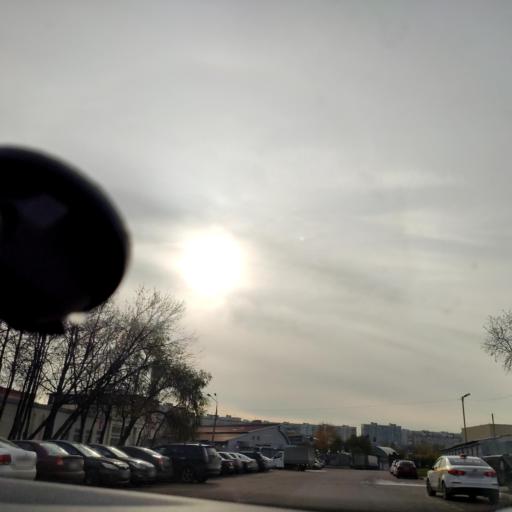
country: RU
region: Moskovskaya
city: Vostochnoe Degunino
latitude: 55.8853
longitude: 37.5529
